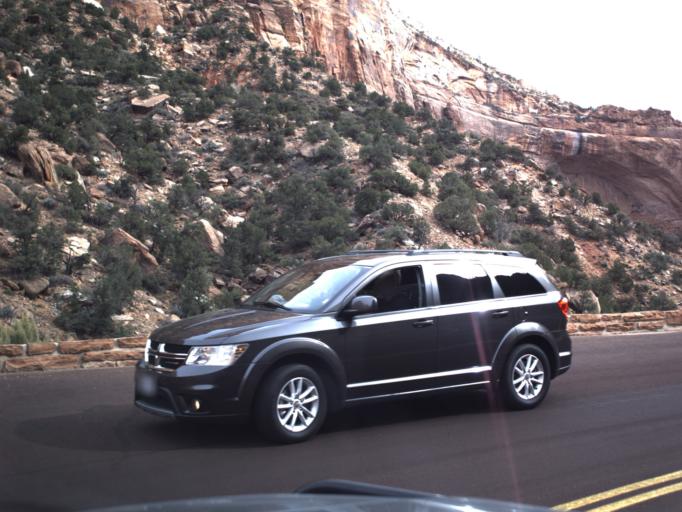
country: US
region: Utah
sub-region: Washington County
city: Hildale
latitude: 37.2145
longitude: -112.9579
